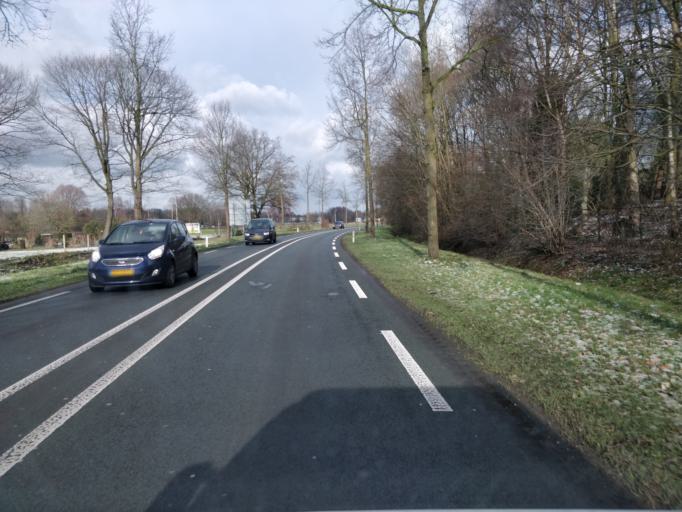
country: NL
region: Gelderland
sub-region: Gemeente Winterswijk
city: Winterswijk
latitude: 51.9676
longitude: 6.6999
